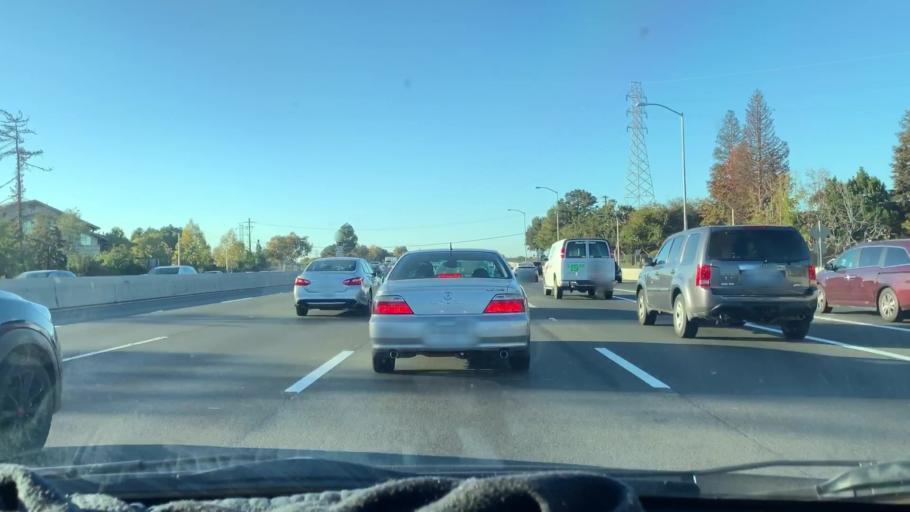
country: US
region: California
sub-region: Santa Clara County
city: Palo Alto
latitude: 37.4301
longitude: -122.1031
